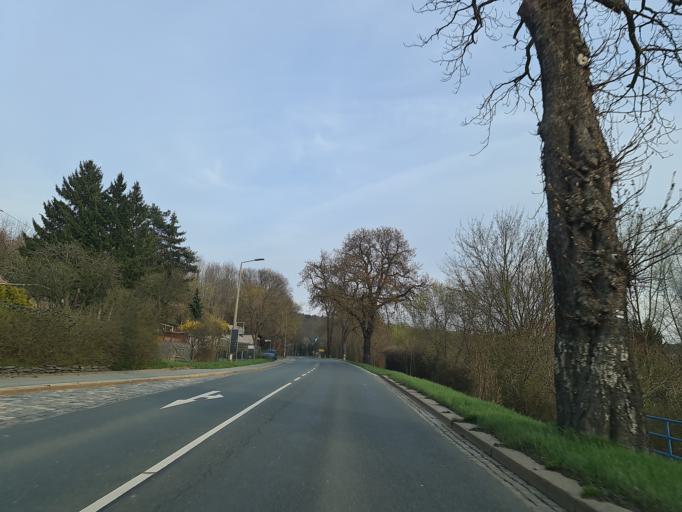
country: DE
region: Saxony
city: Plauen
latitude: 50.4796
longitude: 12.1417
